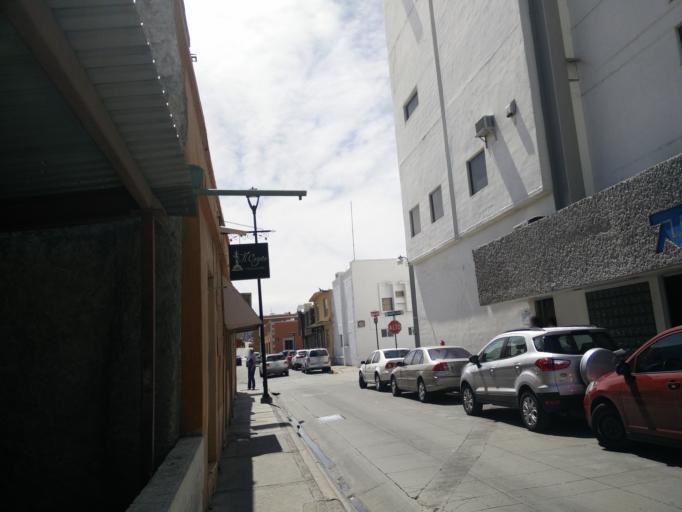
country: MX
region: Chihuahua
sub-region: Chihuahua
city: Chihuahua
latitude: 28.6349
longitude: -106.0756
